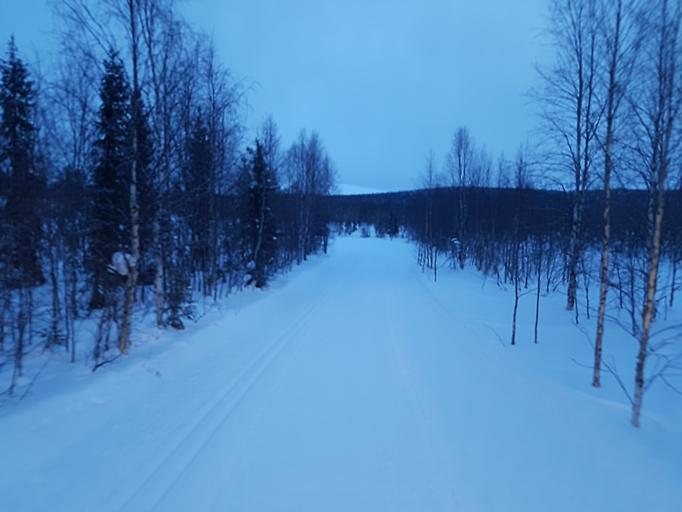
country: FI
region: Lapland
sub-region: Tunturi-Lappi
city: Kolari
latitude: 67.6146
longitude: 24.1554
